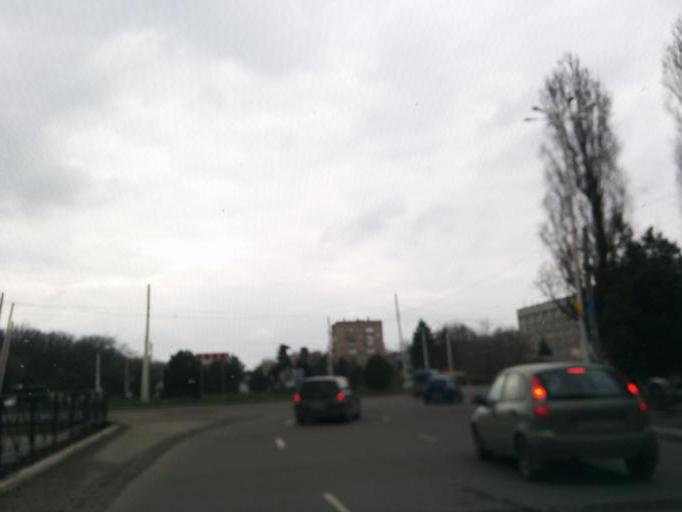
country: RU
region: Rostov
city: Novocherkassk
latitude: 47.4219
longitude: 40.0703
